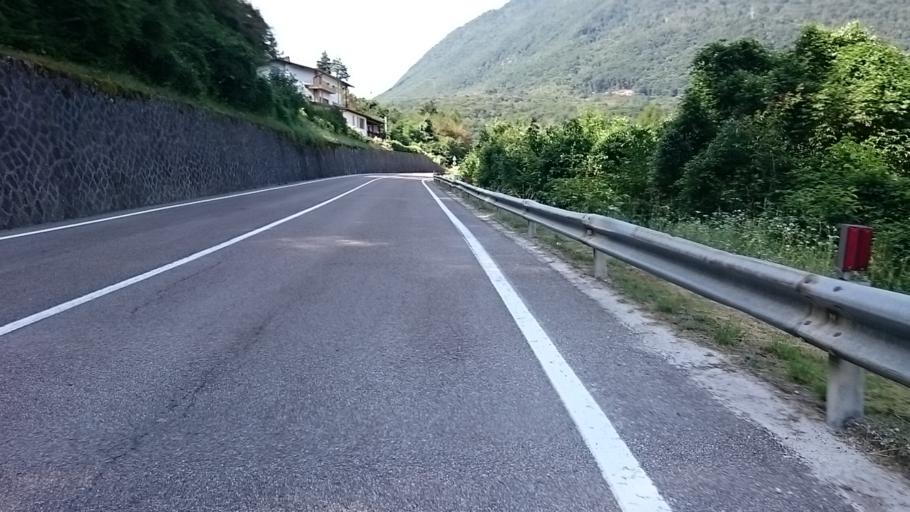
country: IT
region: Veneto
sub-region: Provincia di Belluno
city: Farra d'Alpago
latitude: 46.0887
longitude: 12.3403
